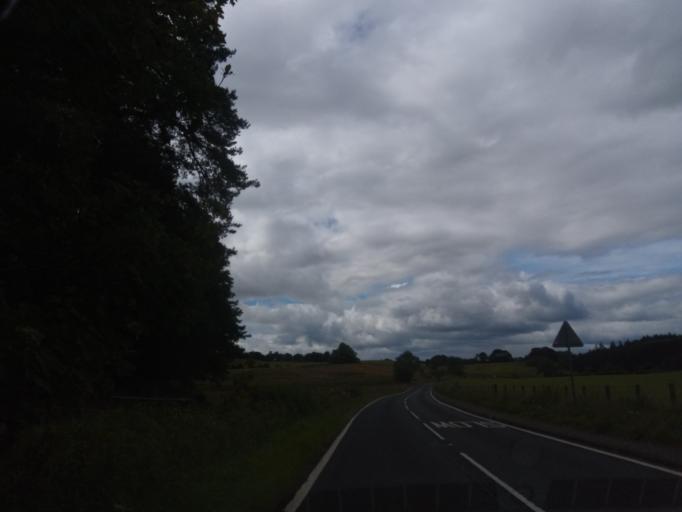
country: GB
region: Scotland
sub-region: Stirling
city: Dunblane
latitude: 56.1910
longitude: -4.0010
